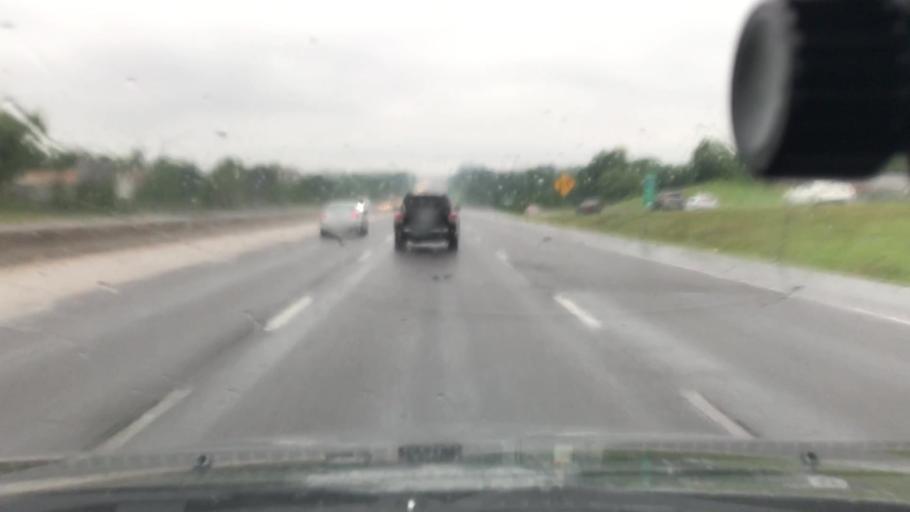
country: US
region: Missouri
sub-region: Saint Louis County
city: Creve Coeur
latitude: 38.6748
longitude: -90.4492
